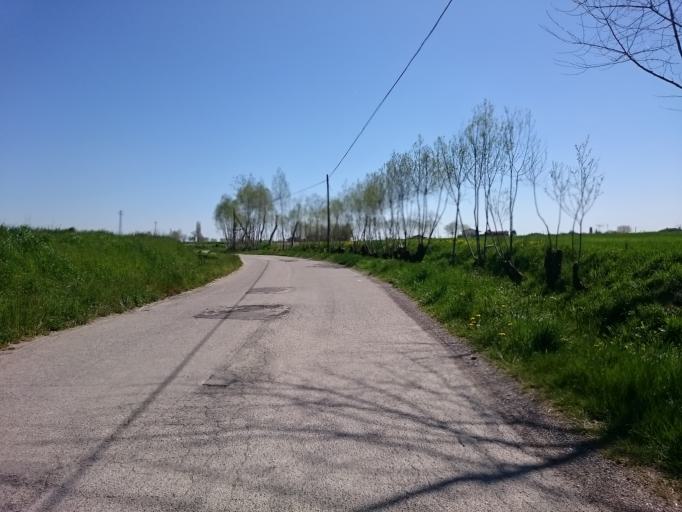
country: IT
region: Veneto
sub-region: Provincia di Padova
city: Brugine
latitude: 45.3073
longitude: 11.9807
